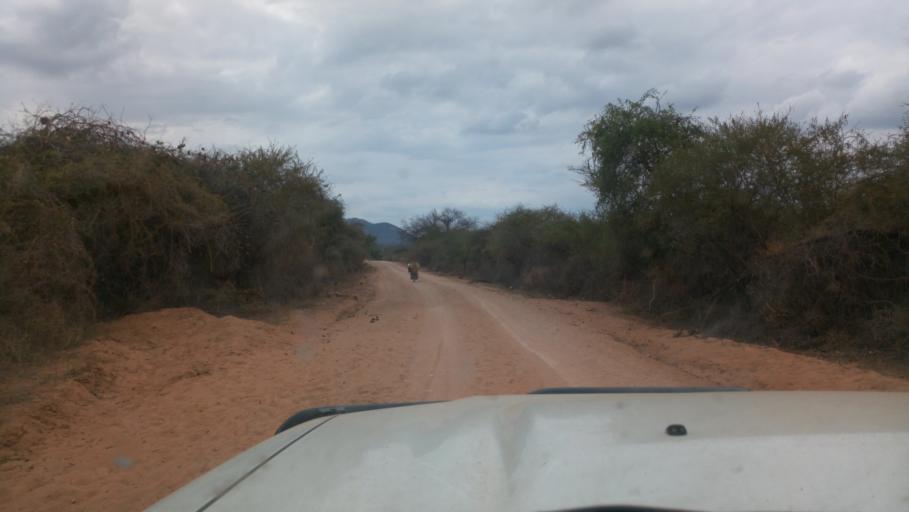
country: KE
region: Kitui
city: Kitui
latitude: -1.8217
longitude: 38.4285
